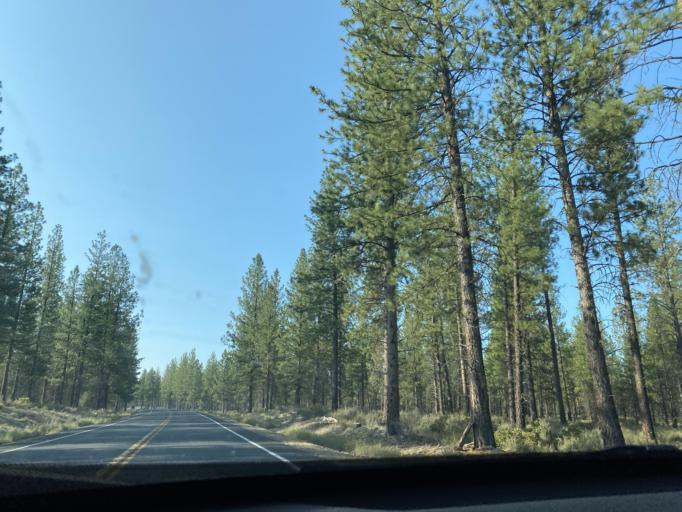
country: US
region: Oregon
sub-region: Deschutes County
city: La Pine
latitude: 43.7205
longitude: -121.4145
